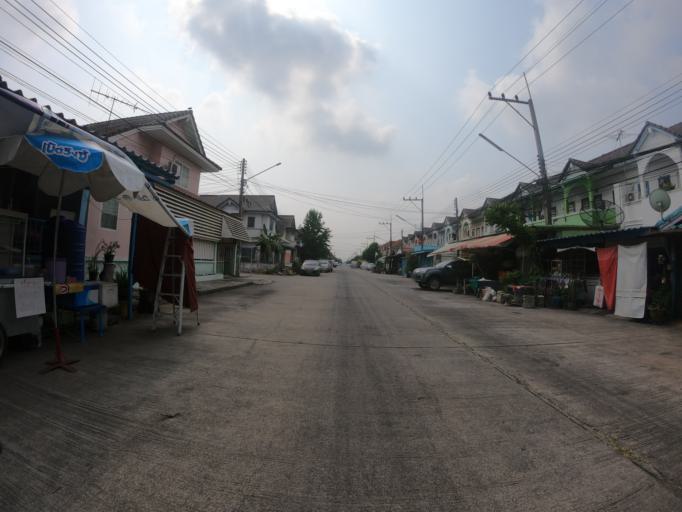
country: TH
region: Pathum Thani
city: Nong Suea
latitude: 14.0739
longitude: 100.8585
